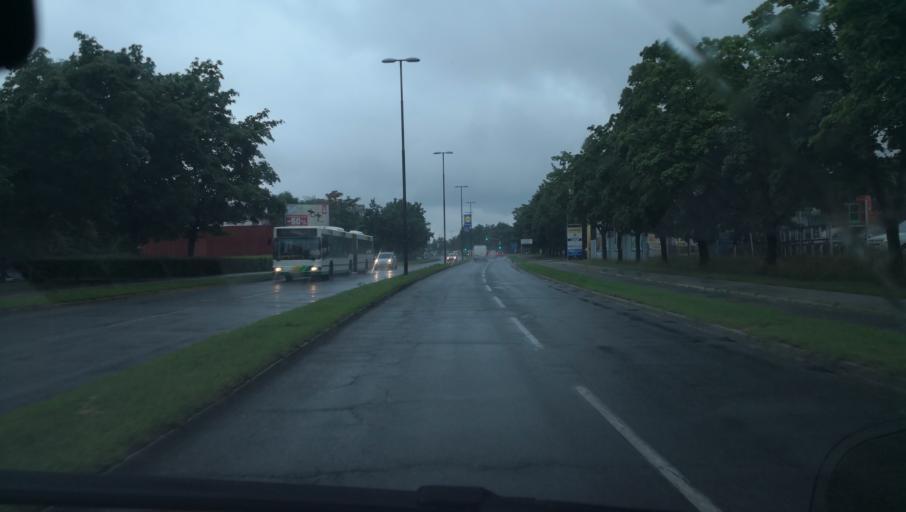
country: SI
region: Dol pri Ljubljani
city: Dol pri Ljubljani
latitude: 46.0552
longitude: 14.5647
